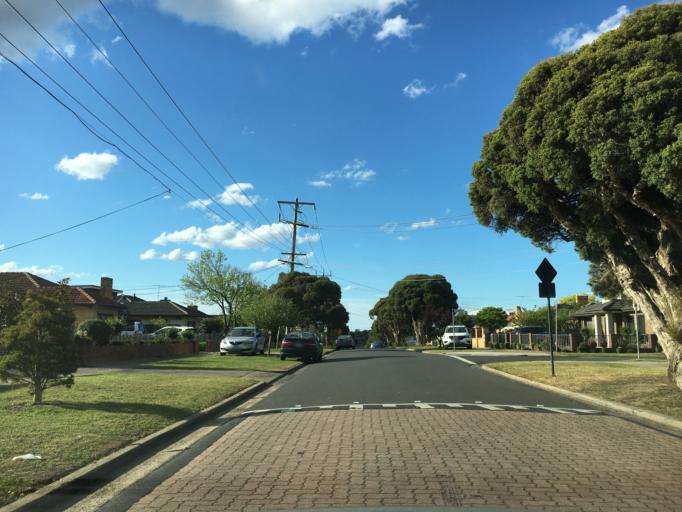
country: AU
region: Victoria
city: Clayton
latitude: -37.9025
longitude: 145.1127
